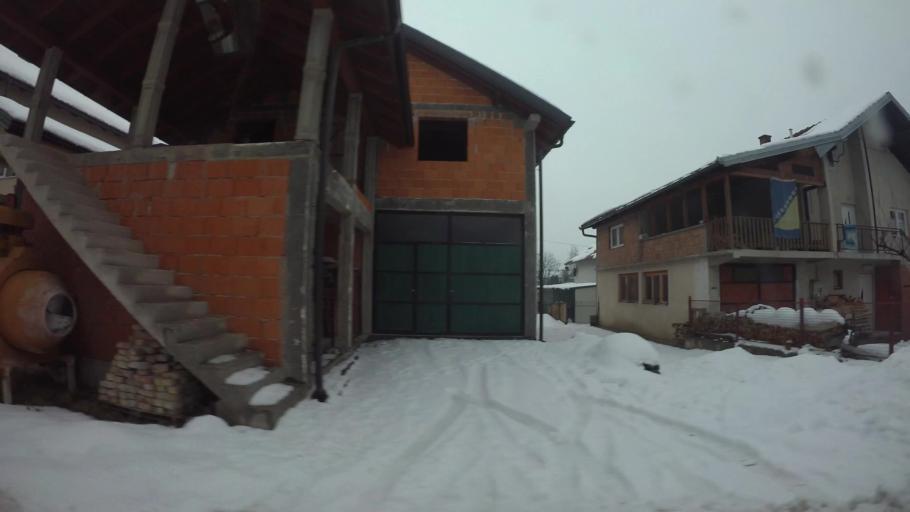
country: BA
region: Federation of Bosnia and Herzegovina
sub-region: Kanton Sarajevo
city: Sarajevo
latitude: 43.8408
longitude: 18.3046
